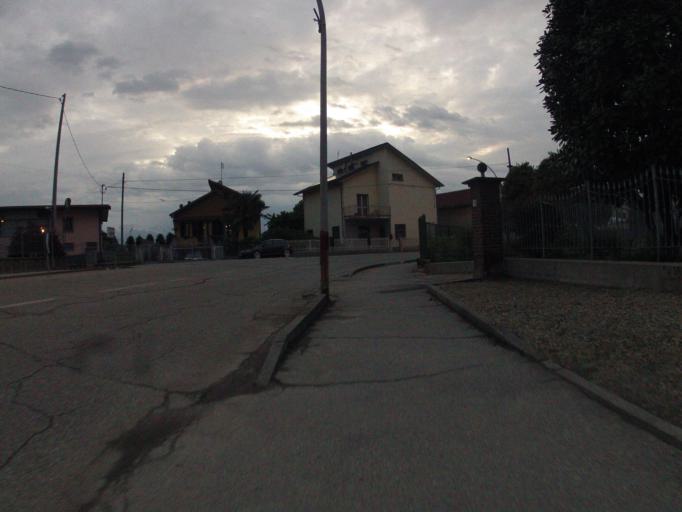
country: IT
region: Piedmont
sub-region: Provincia di Cuneo
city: Moretta
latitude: 44.7646
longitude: 7.5314
